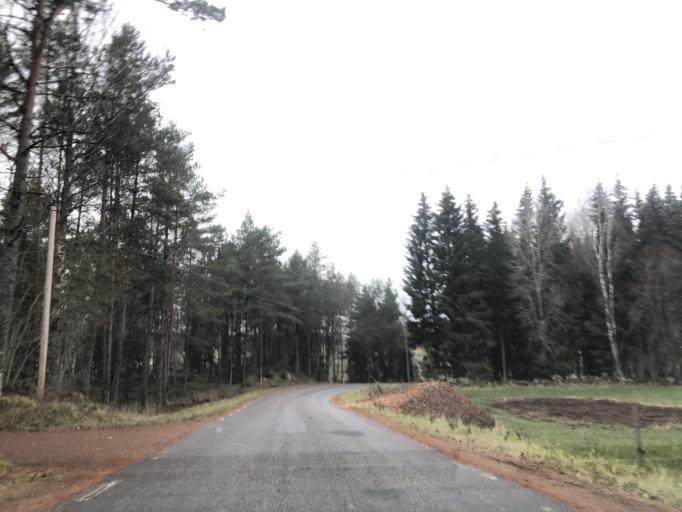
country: SE
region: Vaestra Goetaland
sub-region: Ulricehamns Kommun
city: Ulricehamn
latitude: 57.8722
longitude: 13.5454
